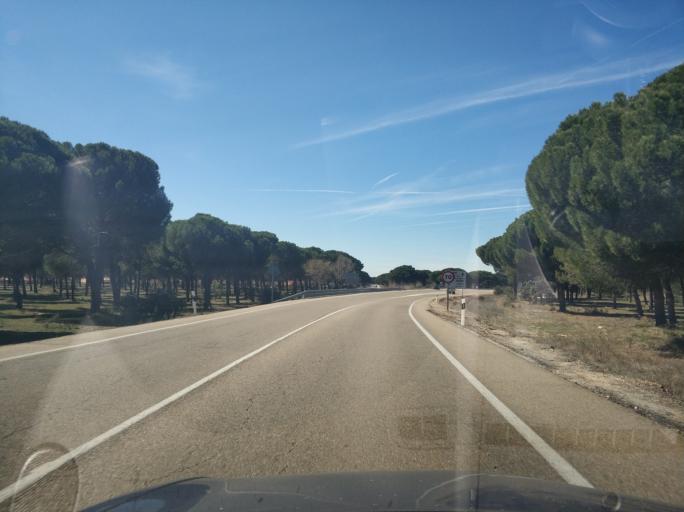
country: ES
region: Castille and Leon
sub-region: Provincia de Valladolid
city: Viana de Cega
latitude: 41.5323
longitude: -4.7256
